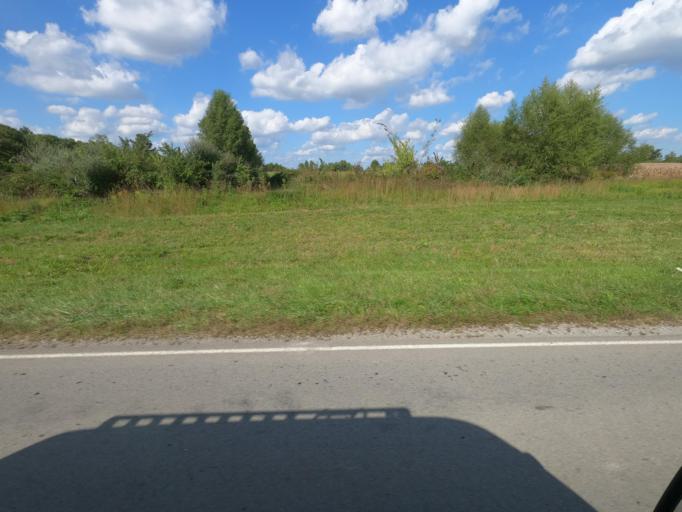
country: US
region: Illinois
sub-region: Massac County
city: Metropolis
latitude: 37.1911
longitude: -88.6894
